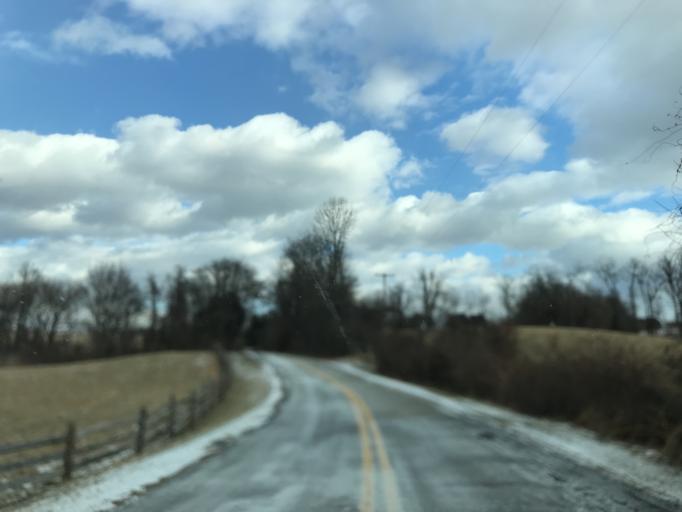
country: US
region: Maryland
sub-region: Harford County
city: Jarrettsville
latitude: 39.6381
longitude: -76.5150
